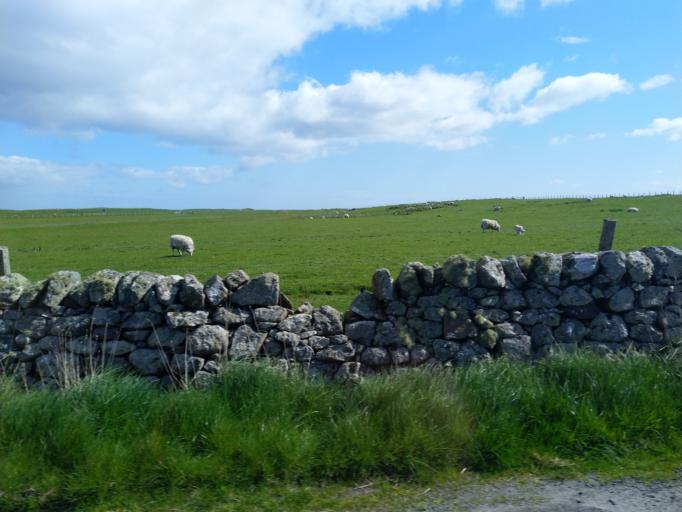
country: GB
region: Scotland
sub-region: Eilean Siar
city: Barra
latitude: 56.4841
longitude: -6.9043
